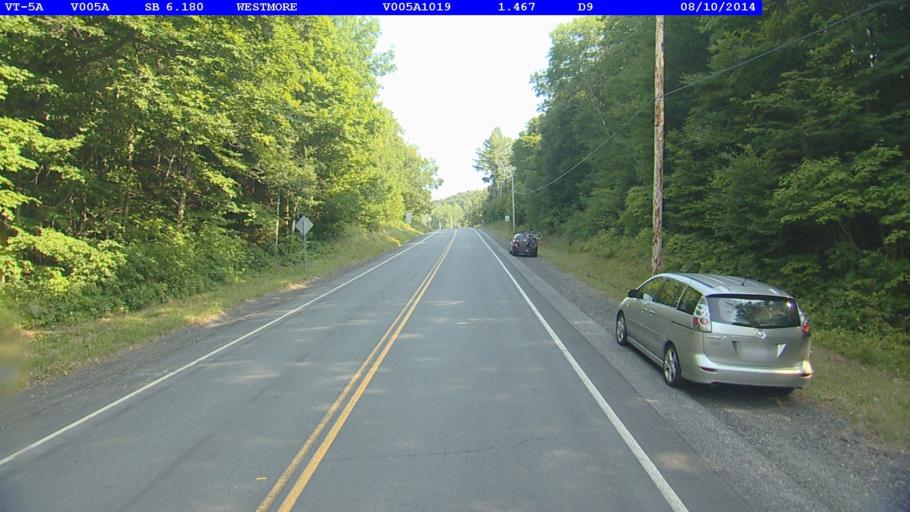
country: US
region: Vermont
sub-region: Caledonia County
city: Lyndonville
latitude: 44.7155
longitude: -72.0300
